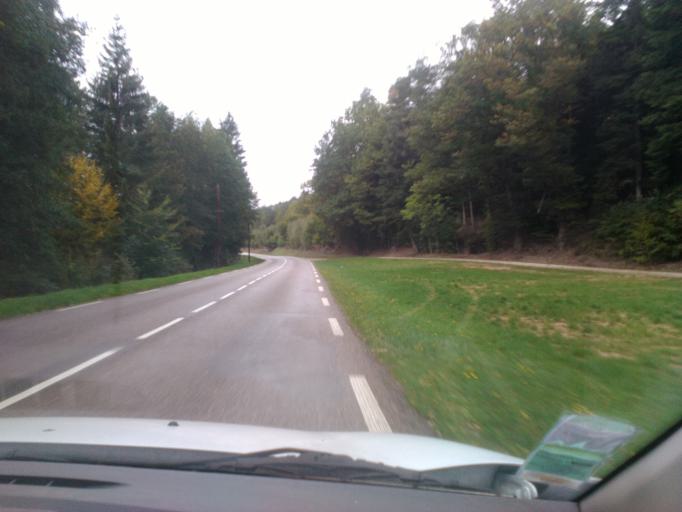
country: FR
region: Lorraine
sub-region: Departement des Vosges
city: Jeanmenil
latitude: 48.3242
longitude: 6.7362
